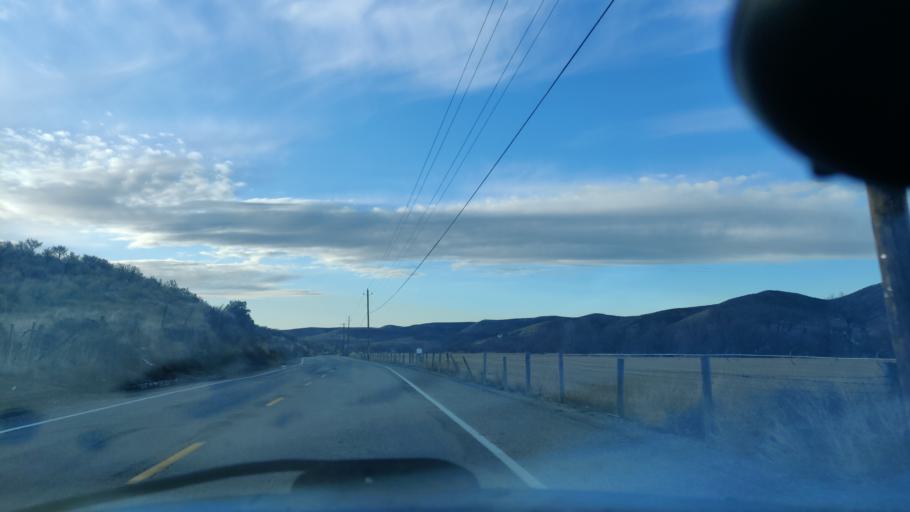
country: US
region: Idaho
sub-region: Ada County
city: Eagle
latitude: 43.7297
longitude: -116.2919
